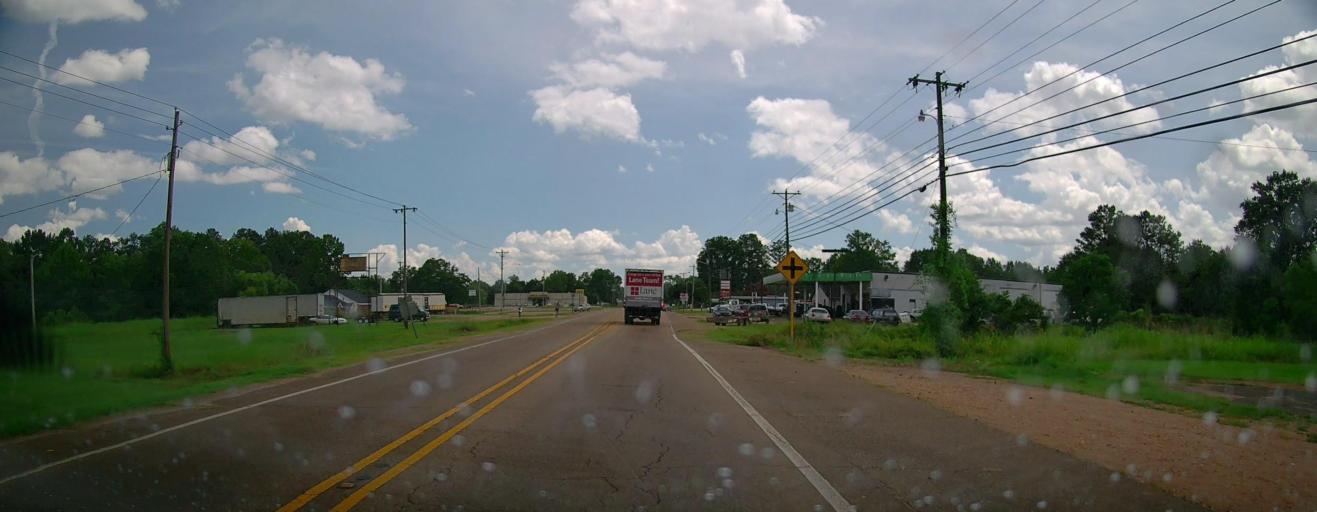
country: US
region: Mississippi
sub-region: Lee County
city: Shannon
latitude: 34.1280
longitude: -88.7193
